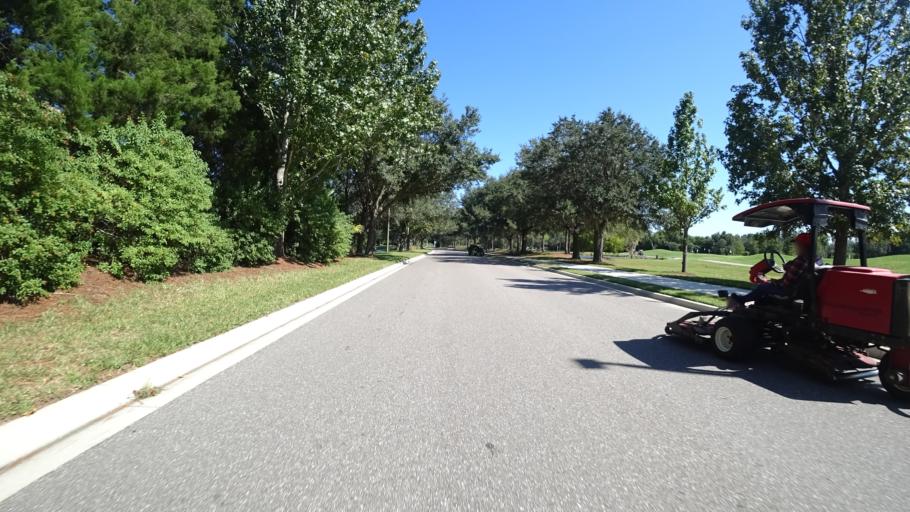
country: US
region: Florida
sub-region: Sarasota County
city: The Meadows
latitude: 27.3947
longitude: -82.4038
